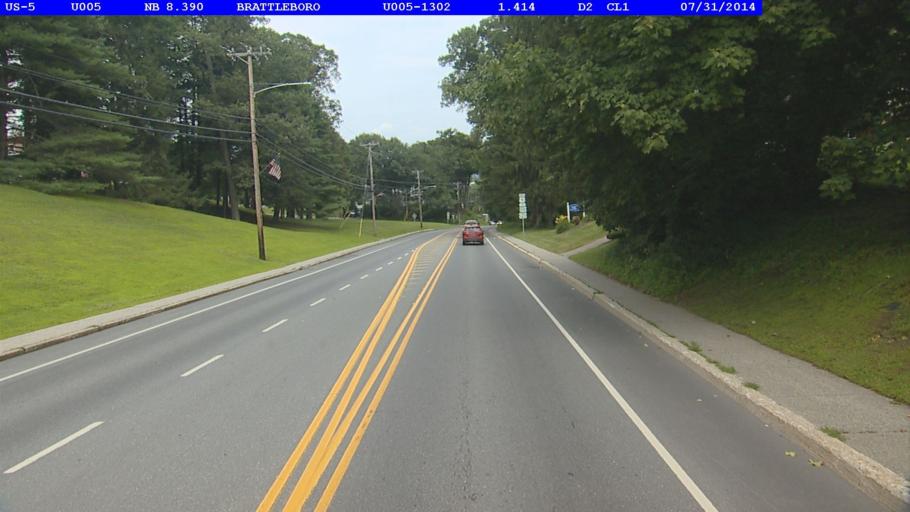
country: US
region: Vermont
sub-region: Windham County
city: Brattleboro
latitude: 42.8423
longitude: -72.5639
